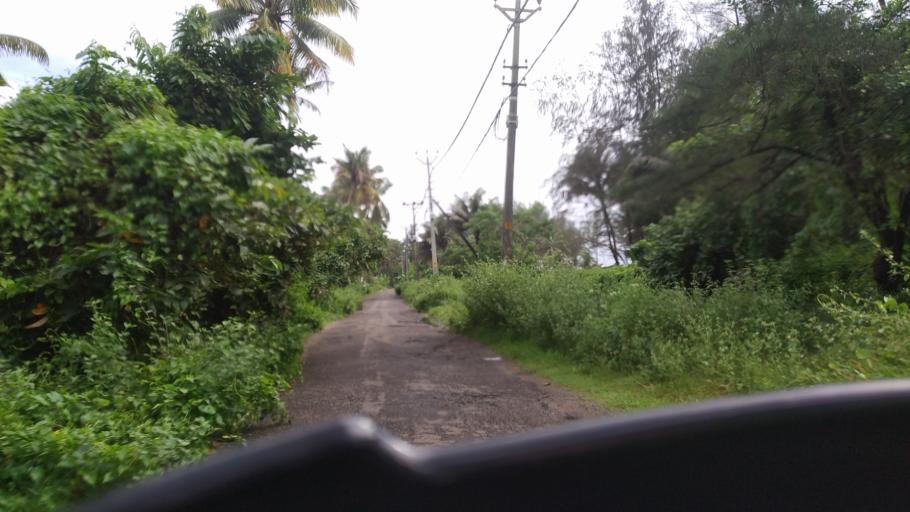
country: IN
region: Kerala
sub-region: Thrissur District
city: Kodungallur
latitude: 10.1161
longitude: 76.1862
